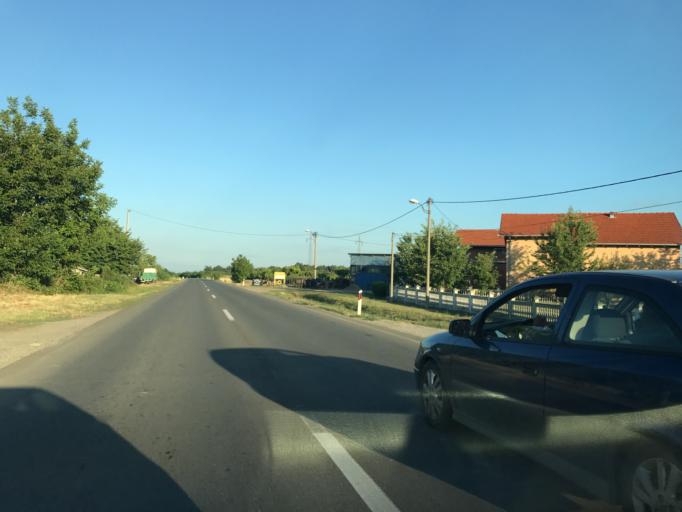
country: RS
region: Central Serbia
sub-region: Podunavski Okrug
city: Smederevo
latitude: 44.6147
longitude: 20.9027
